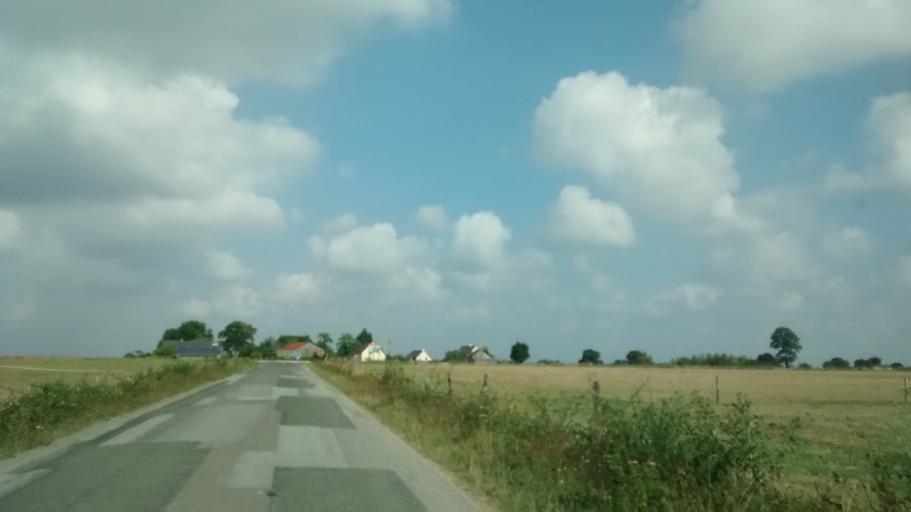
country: FR
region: Brittany
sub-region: Departement d'Ille-et-Vilaine
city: Erbree
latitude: 48.1325
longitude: -1.1007
